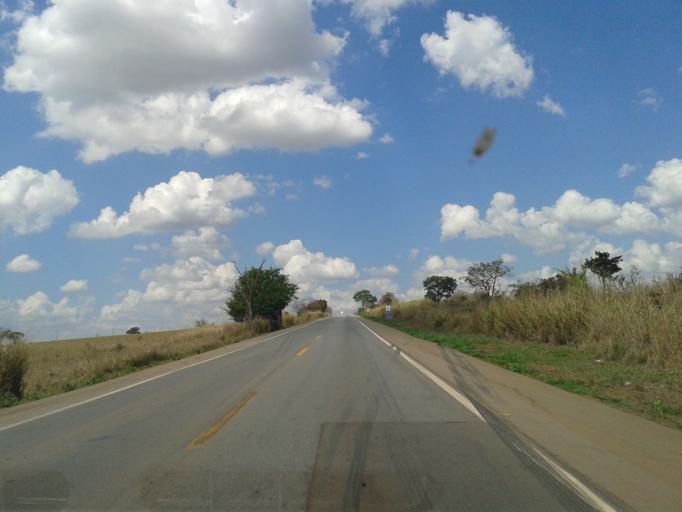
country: BR
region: Minas Gerais
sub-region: Luz
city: Luz
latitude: -19.7840
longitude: -45.7025
